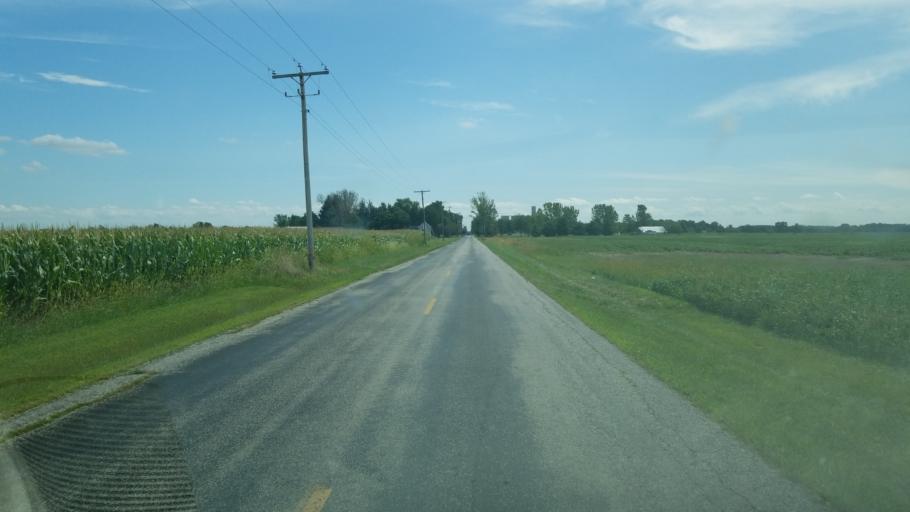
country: US
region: Ohio
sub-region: Union County
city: Richwood
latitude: 40.5956
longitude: -83.3147
